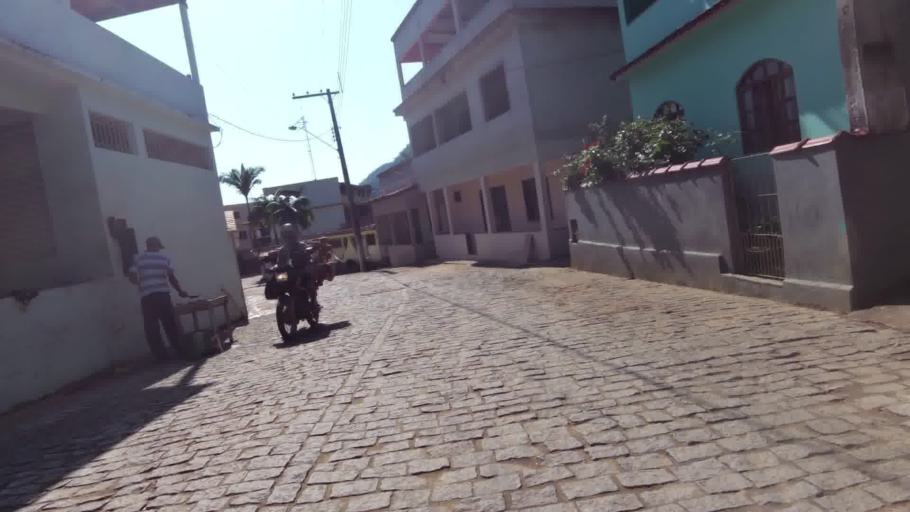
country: BR
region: Espirito Santo
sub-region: Alfredo Chaves
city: Alfredo Chaves
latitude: -20.6802
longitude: -40.7728
